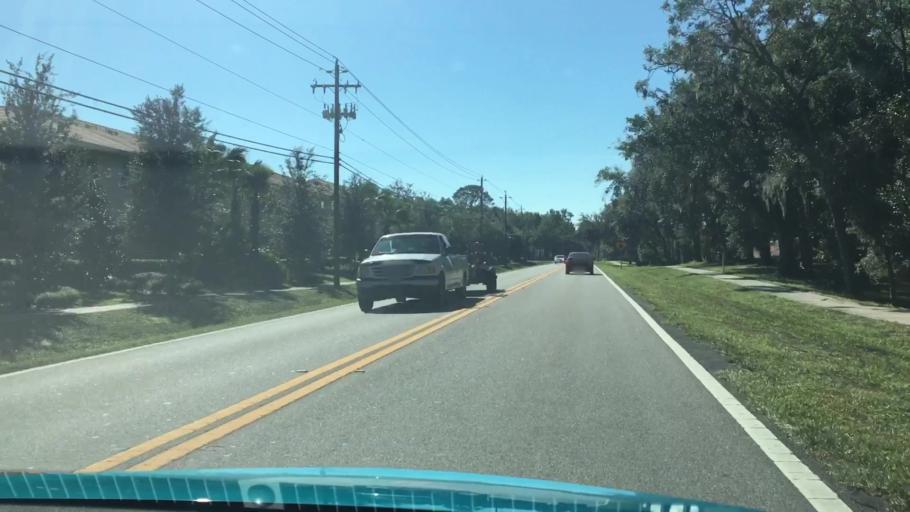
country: US
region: Florida
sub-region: Seminole County
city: Heathrow
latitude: 28.7885
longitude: -81.3629
